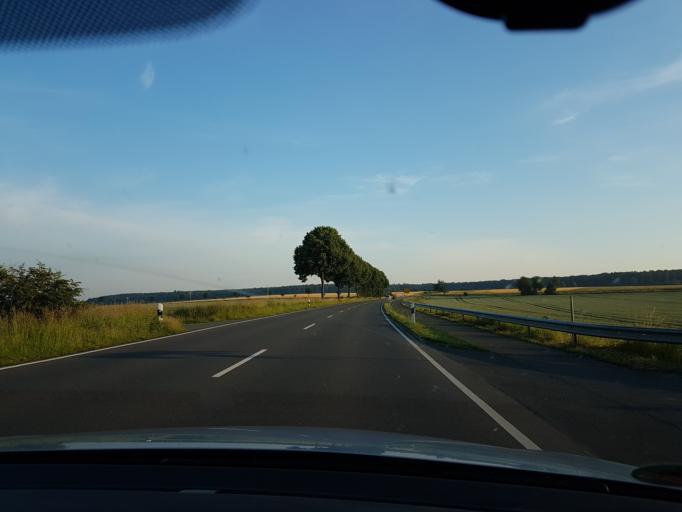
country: DE
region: Lower Saxony
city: Wolsdorf
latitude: 52.1922
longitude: 10.9708
